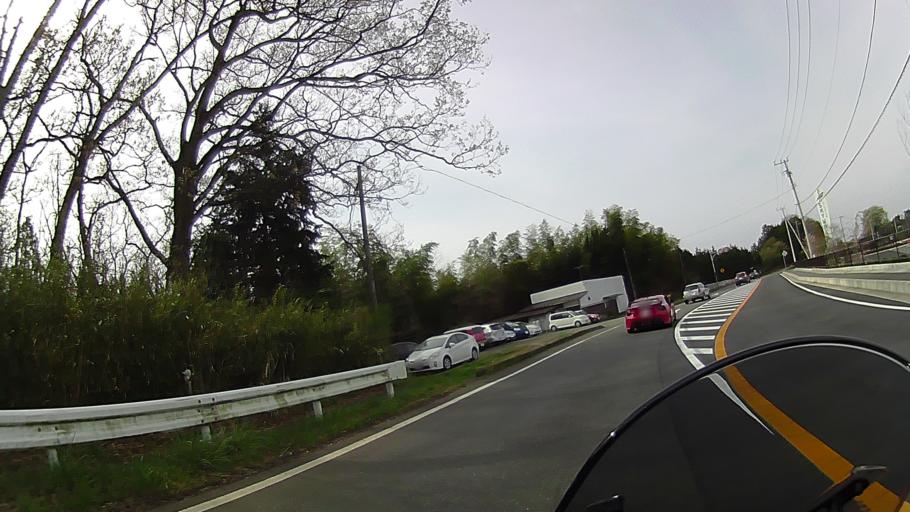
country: JP
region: Kanagawa
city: Hakone
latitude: 35.1495
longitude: 138.9835
